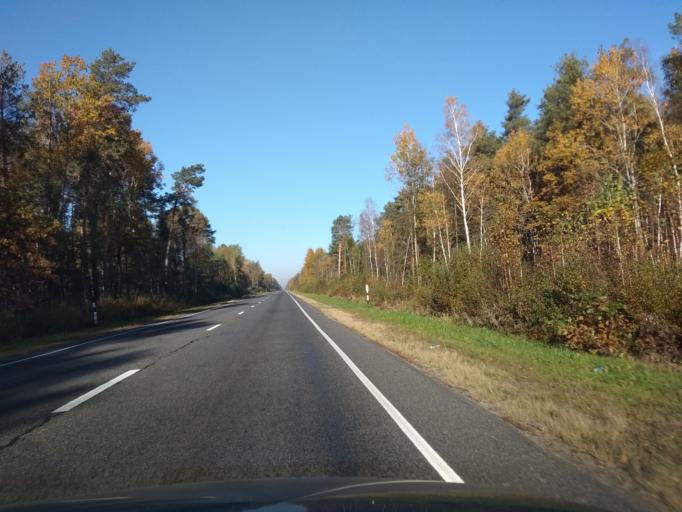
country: BY
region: Brest
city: Malaryta
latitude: 51.8957
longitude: 24.1328
